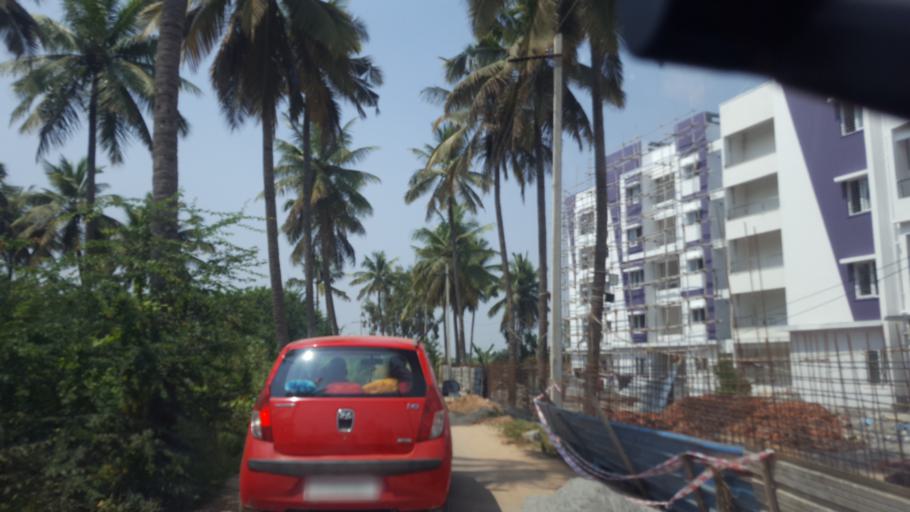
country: IN
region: Karnataka
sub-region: Bangalore Urban
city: Bangalore
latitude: 12.9385
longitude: 77.7116
